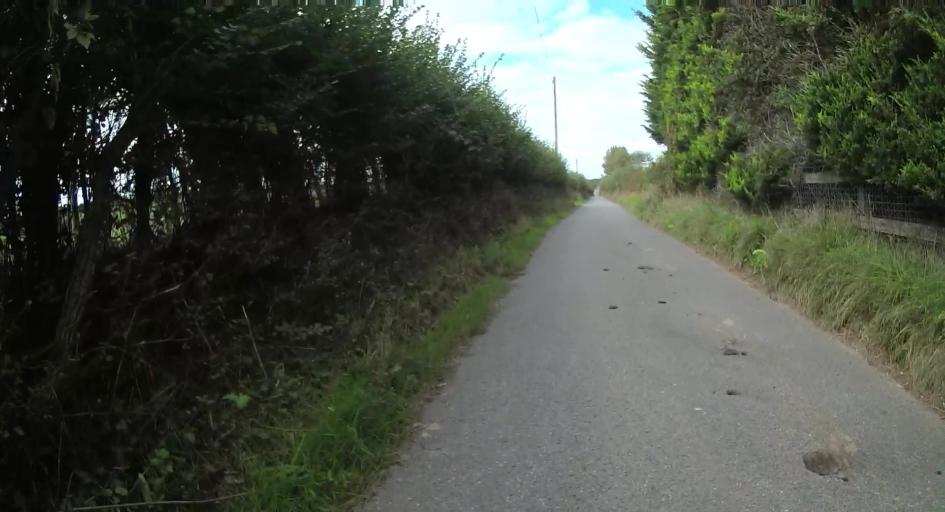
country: GB
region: England
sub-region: Isle of Wight
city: Niton
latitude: 50.6308
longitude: -1.2686
